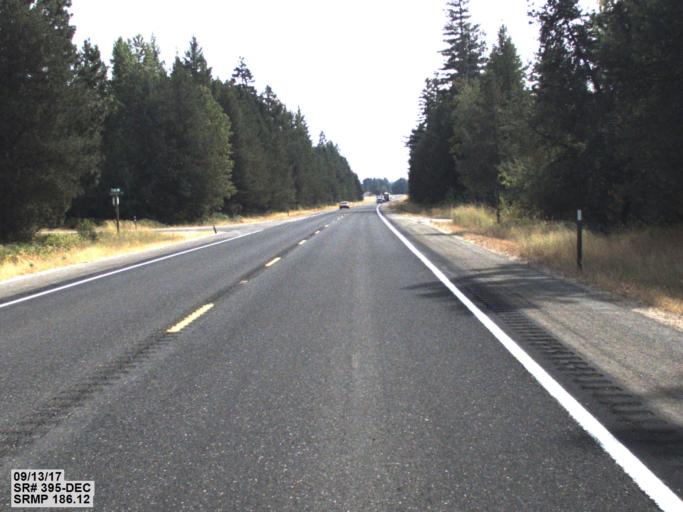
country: US
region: Washington
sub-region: Spokane County
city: Deer Park
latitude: 48.0039
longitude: -117.5770
